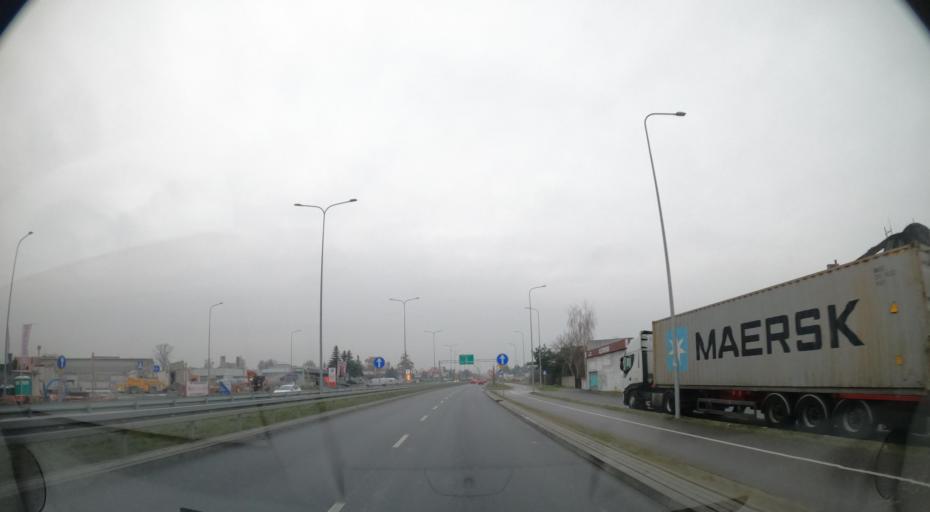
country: PL
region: Masovian Voivodeship
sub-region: Radom
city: Radom
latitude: 51.3829
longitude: 21.1833
